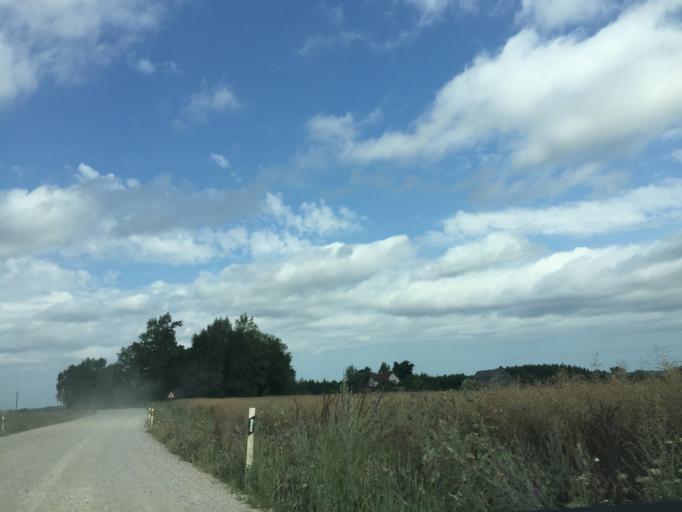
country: LV
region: Kandava
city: Kandava
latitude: 56.9872
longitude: 22.9037
